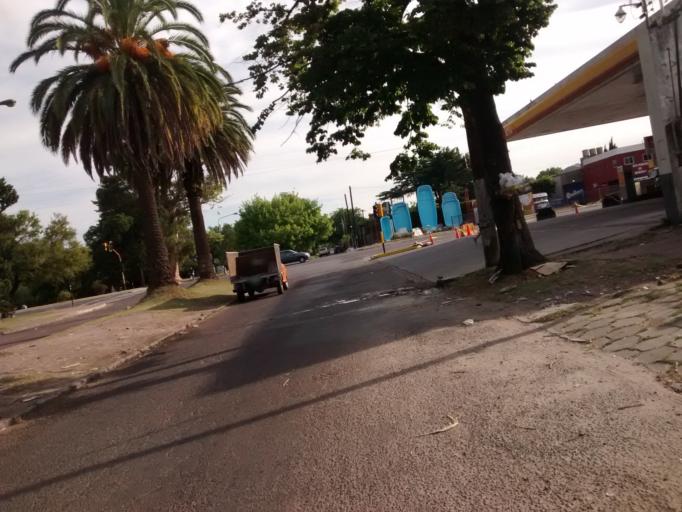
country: AR
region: Buenos Aires
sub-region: Partido de La Plata
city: La Plata
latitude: -34.8506
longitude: -58.0882
